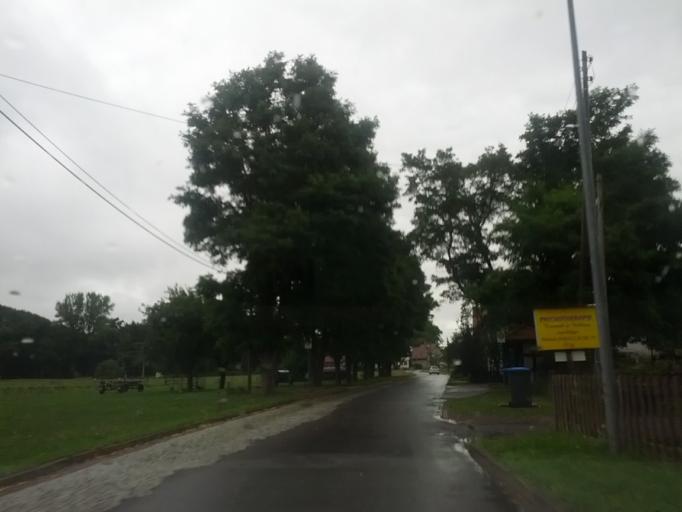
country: DE
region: Thuringia
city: Mechterstadt
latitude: 50.9339
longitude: 10.4814
